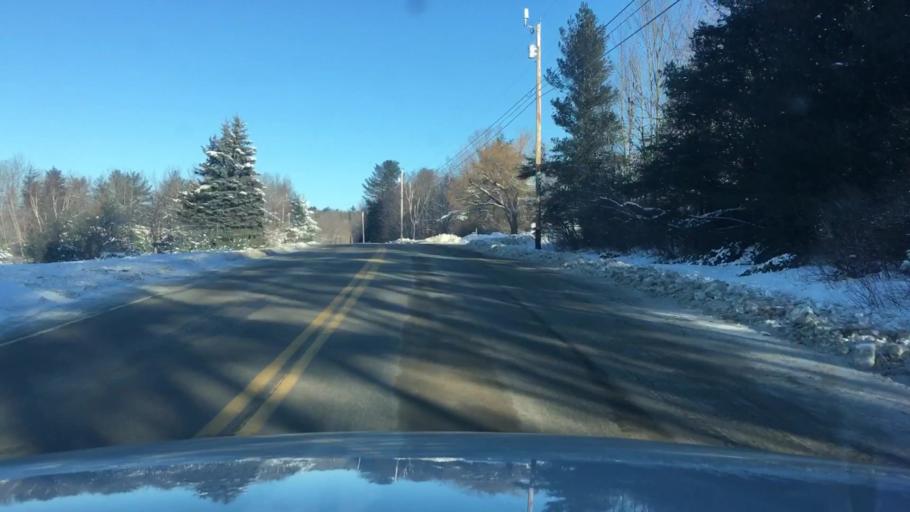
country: US
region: Maine
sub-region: Kennebec County
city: Readfield
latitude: 44.4455
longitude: -69.9684
